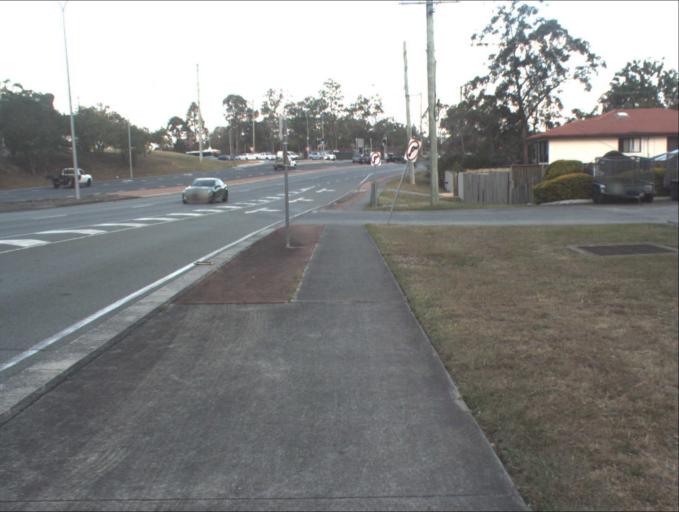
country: AU
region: Queensland
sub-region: Logan
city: Beenleigh
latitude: -27.6705
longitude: 153.2009
